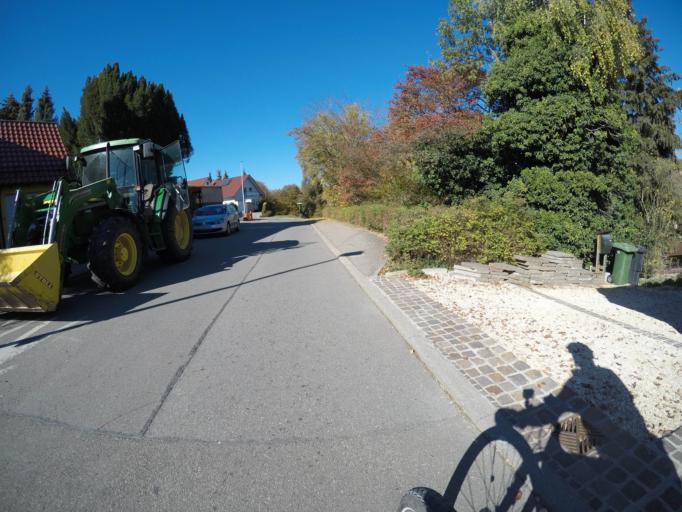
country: DE
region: Baden-Wuerttemberg
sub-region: Tuebingen Region
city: Rottenburg
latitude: 48.5351
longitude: 8.9452
